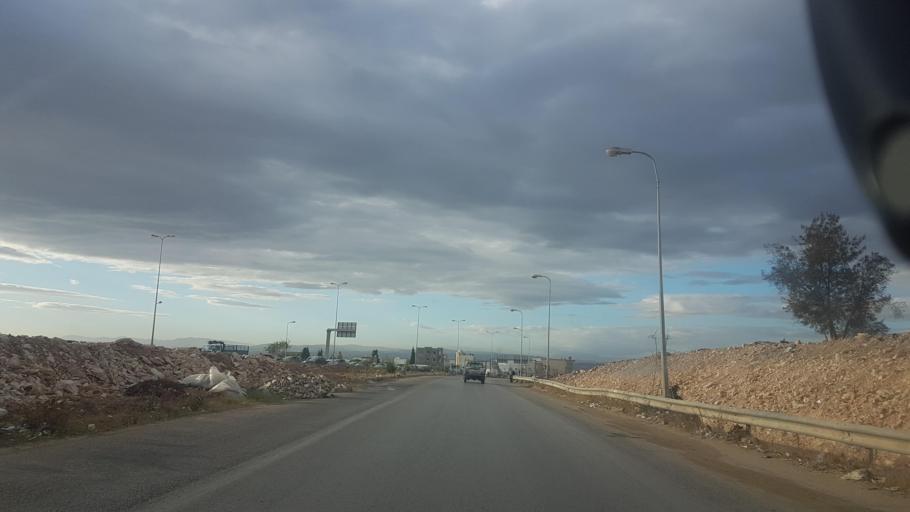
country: TN
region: Bin 'Arus
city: Ben Arous
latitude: 36.7457
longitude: 10.2082
